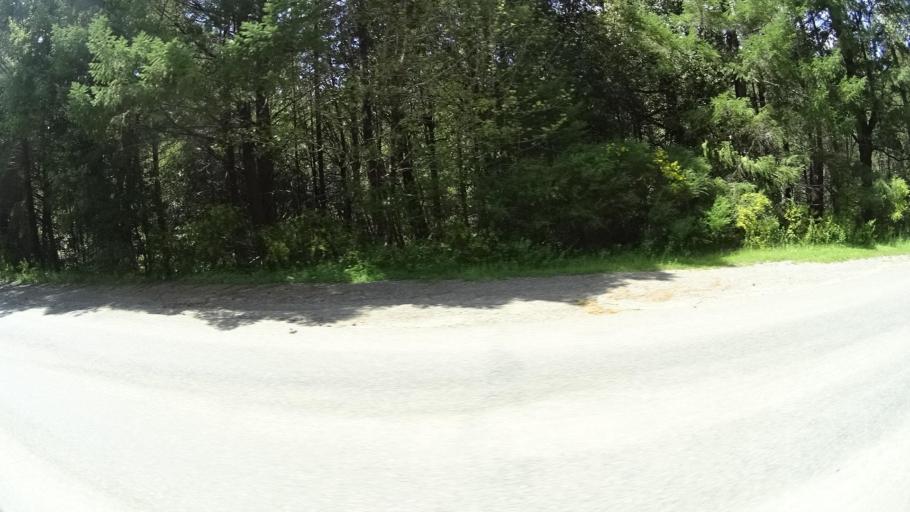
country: US
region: California
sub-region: Humboldt County
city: Redway
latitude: 40.0966
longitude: -123.9309
